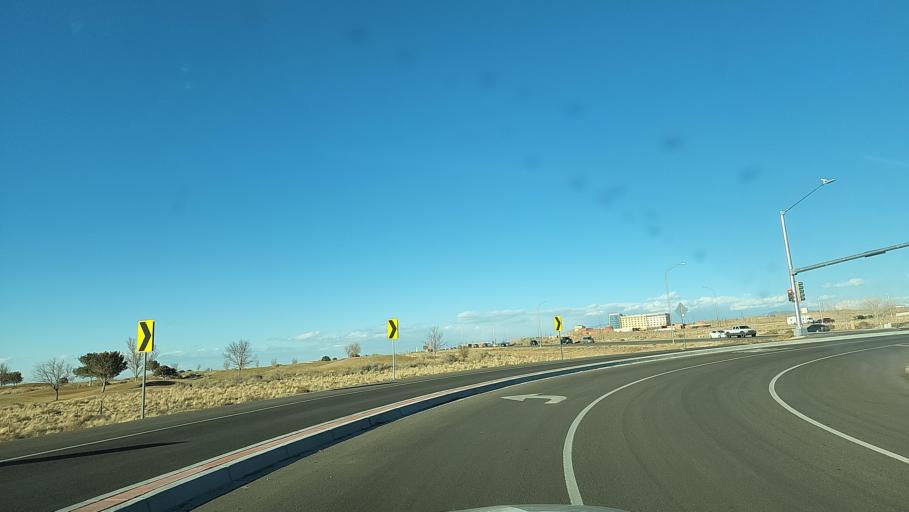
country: US
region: New Mexico
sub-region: Bernalillo County
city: South Valley
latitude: 34.9298
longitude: -106.6680
